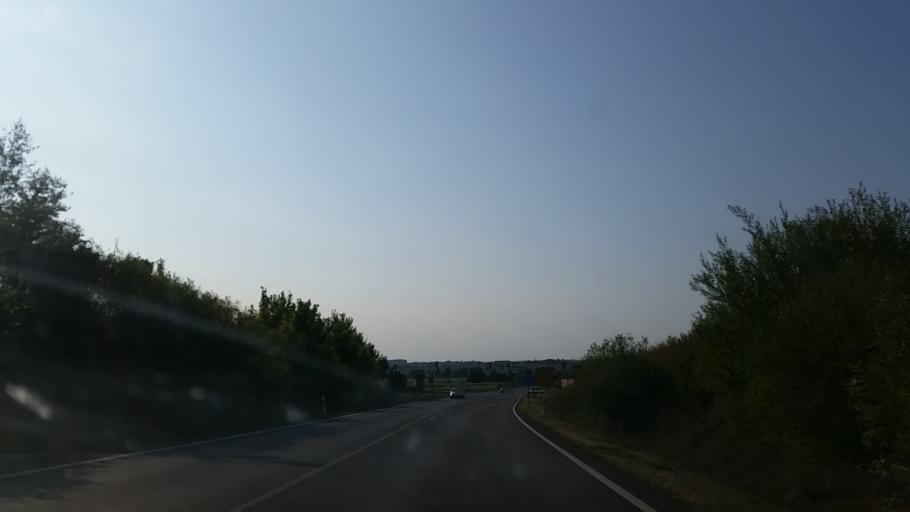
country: DE
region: Brandenburg
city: Passow
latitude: 53.1373
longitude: 14.1050
